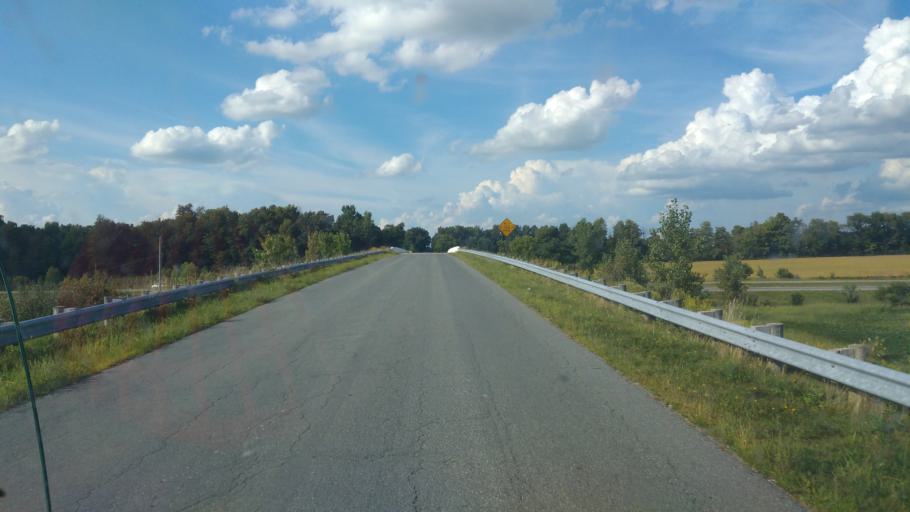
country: US
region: Ohio
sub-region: Crawford County
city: Galion
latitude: 40.7606
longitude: -82.7830
